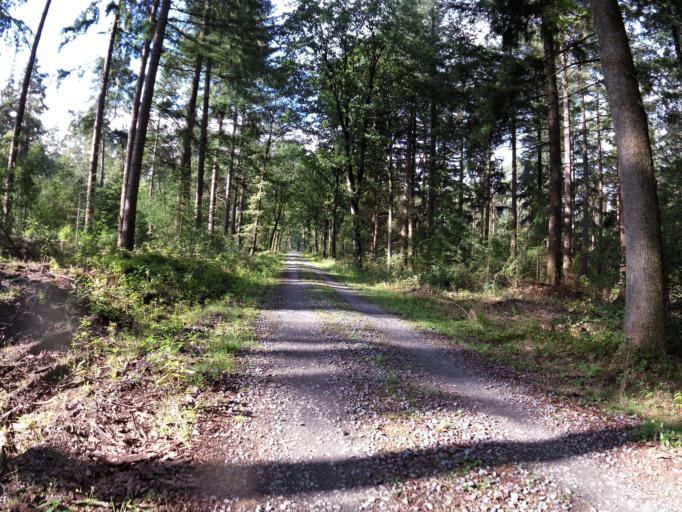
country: DE
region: Lower Saxony
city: Bremervorde
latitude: 53.4756
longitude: 9.1518
